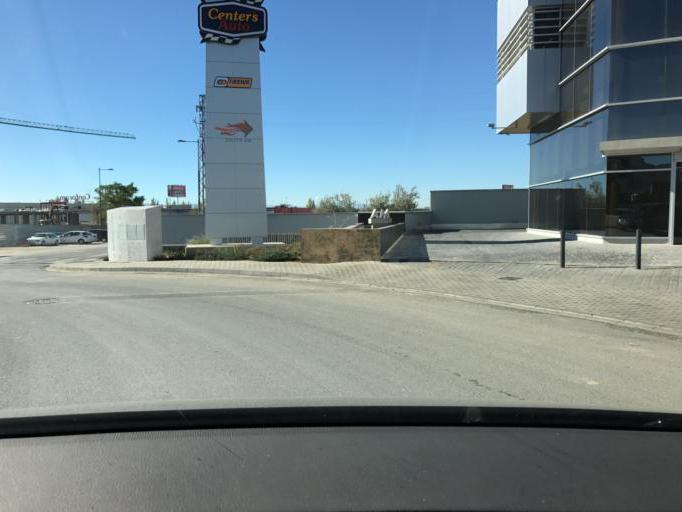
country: ES
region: Andalusia
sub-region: Provincia de Granada
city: Pulianas
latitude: 37.2148
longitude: -3.6213
